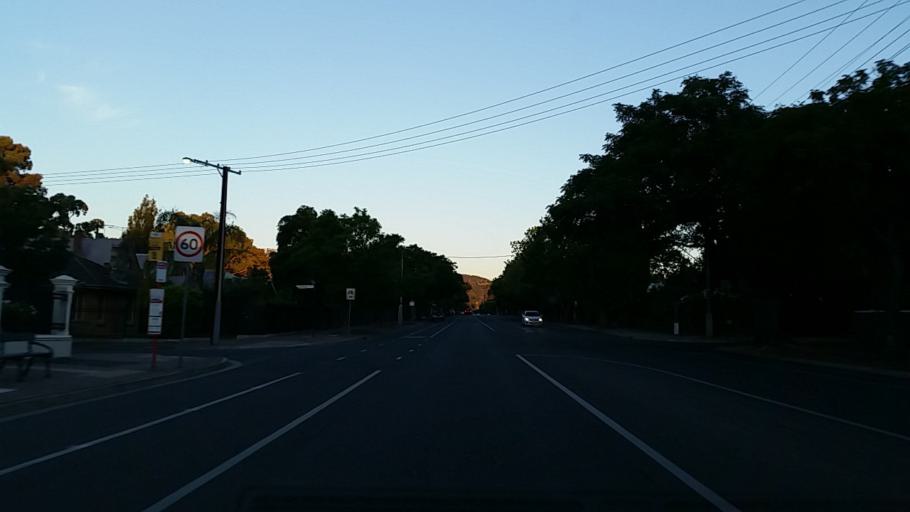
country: AU
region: South Australia
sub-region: Burnside
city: Kensington Gardens
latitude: -34.9202
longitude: 138.6554
